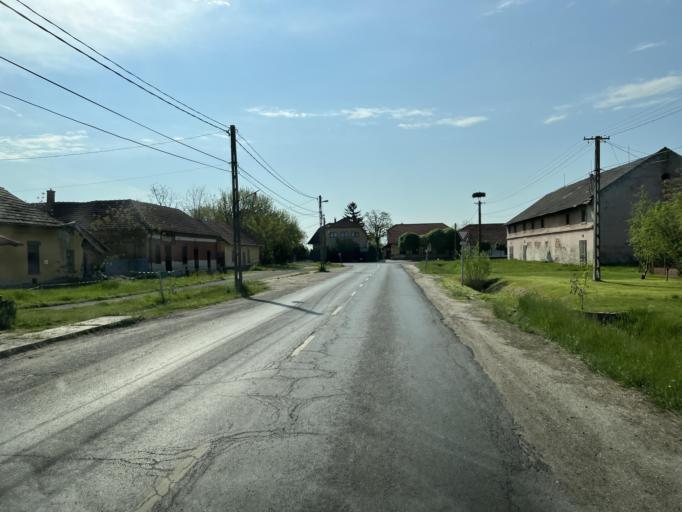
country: HU
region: Pest
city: Jaszkarajeno
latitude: 47.0487
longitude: 20.0733
